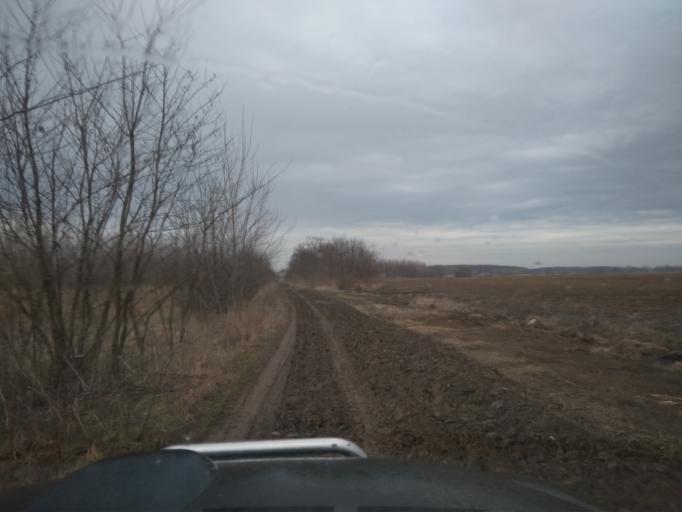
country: HU
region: Szabolcs-Szatmar-Bereg
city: Apagy
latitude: 47.9718
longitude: 21.9199
